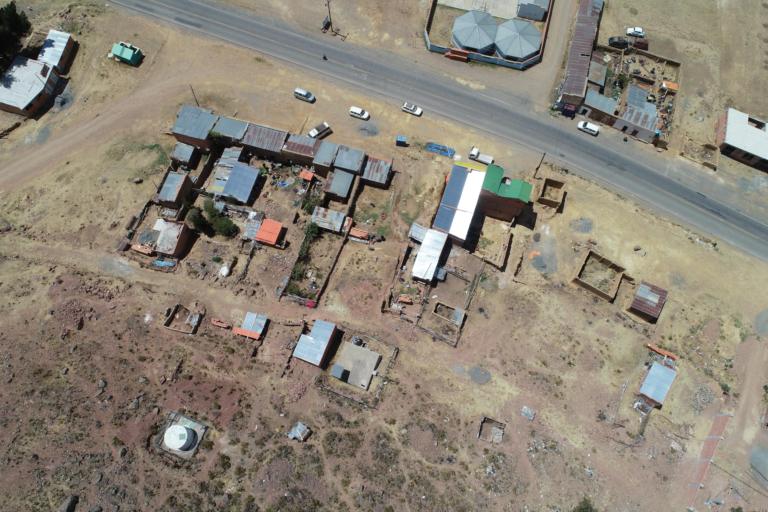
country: BO
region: La Paz
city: Achacachi
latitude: -15.9107
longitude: -68.8856
